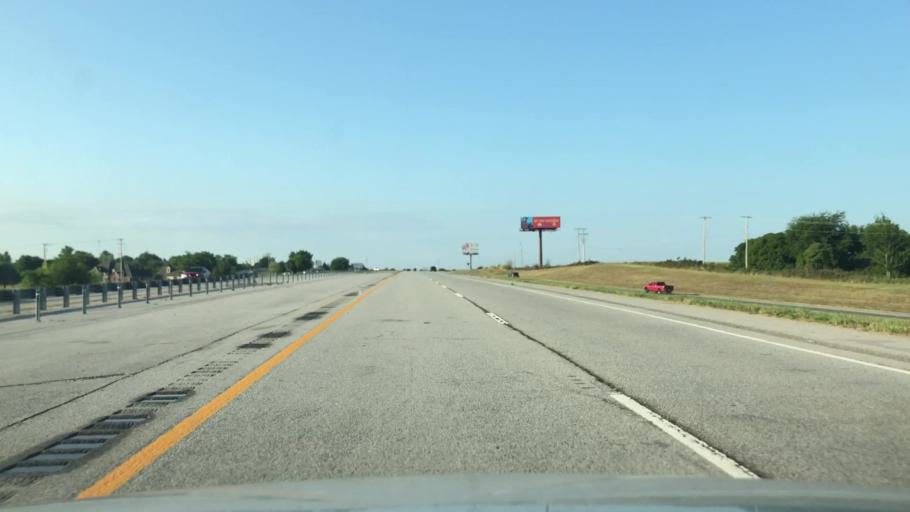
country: US
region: Oklahoma
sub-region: Osage County
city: Skiatook
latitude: 36.3650
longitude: -95.9208
